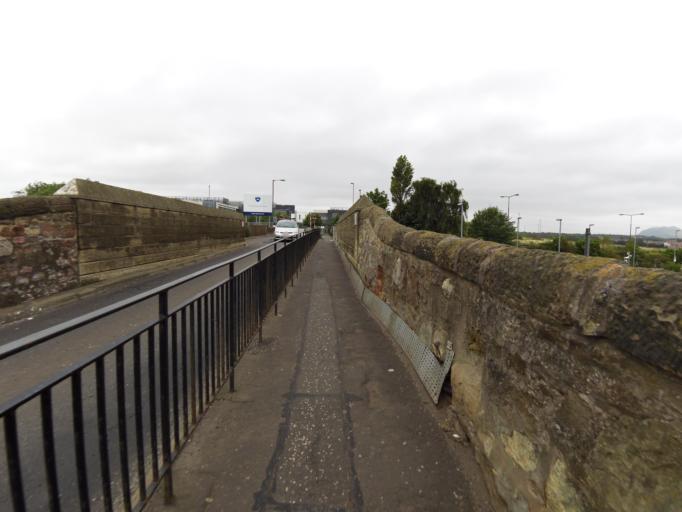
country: GB
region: Scotland
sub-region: East Lothian
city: Musselburgh
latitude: 55.9332
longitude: -3.0714
